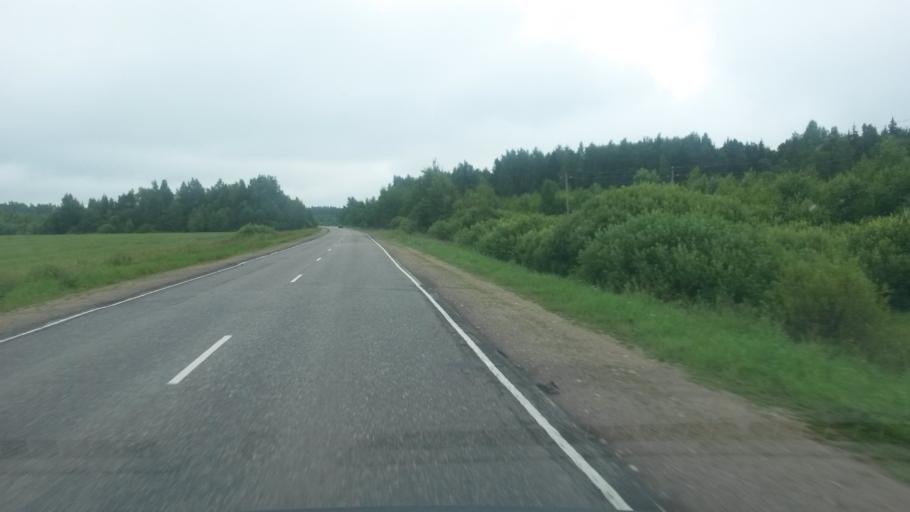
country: RU
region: Ivanovo
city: Novo-Talitsy
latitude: 57.0391
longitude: 40.7440
